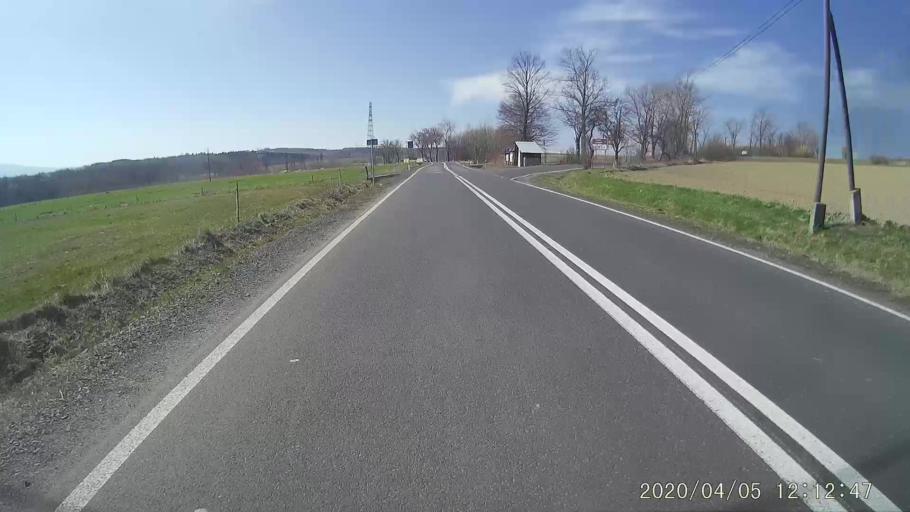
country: PL
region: Lower Silesian Voivodeship
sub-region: Powiat lwowecki
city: Mirsk
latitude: 51.0085
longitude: 15.3639
